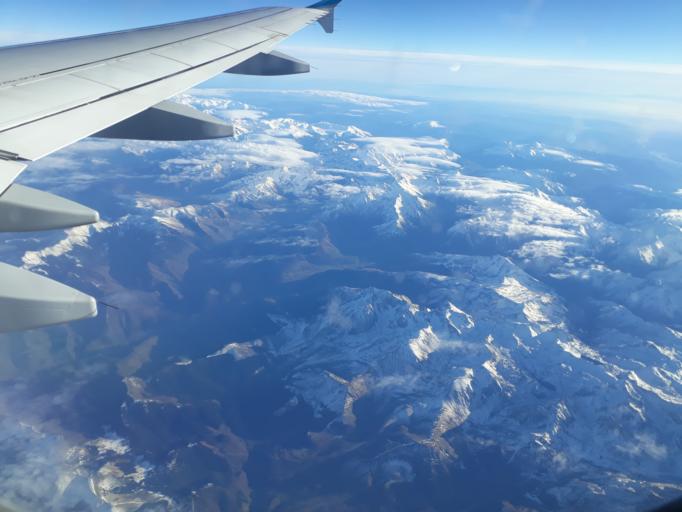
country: FR
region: Midi-Pyrenees
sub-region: Departement des Hautes-Pyrenees
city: Campan
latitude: 43.0239
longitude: 0.1802
